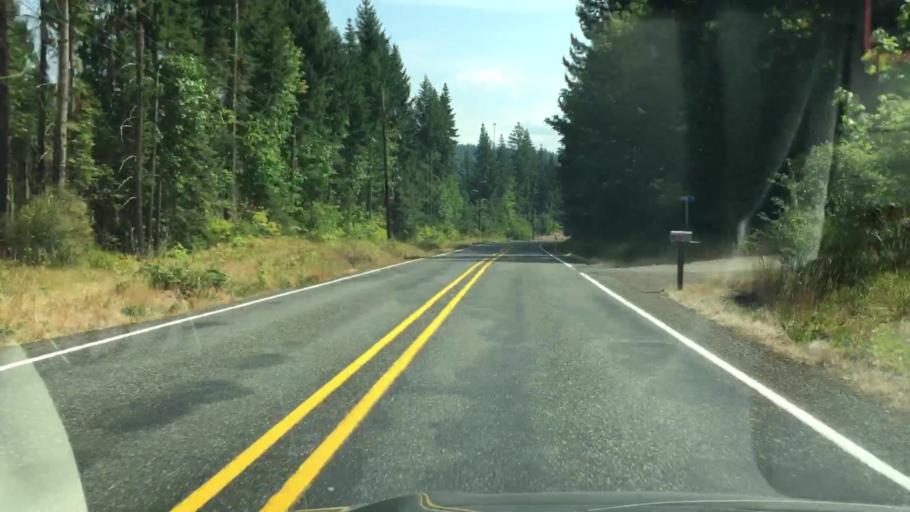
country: US
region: Washington
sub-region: Klickitat County
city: White Salmon
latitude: 45.8686
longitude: -121.5128
